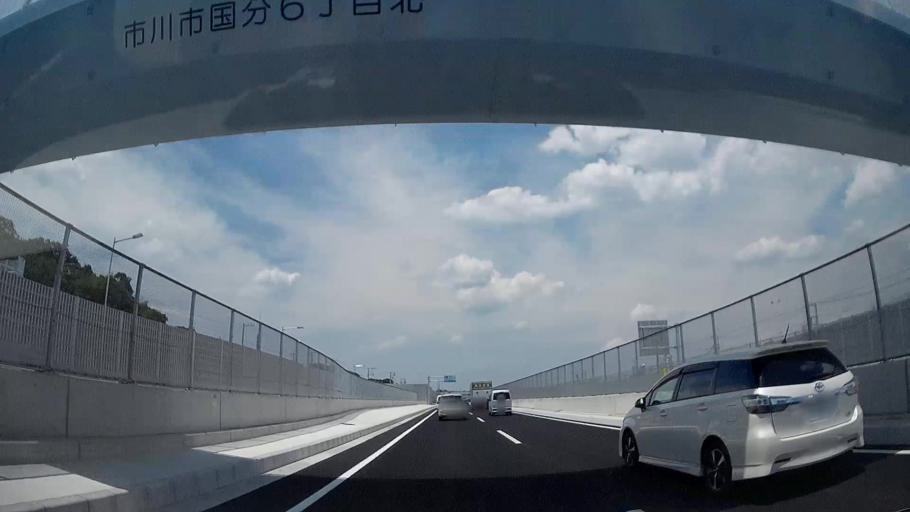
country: JP
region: Chiba
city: Matsudo
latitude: 35.7462
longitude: 139.9194
